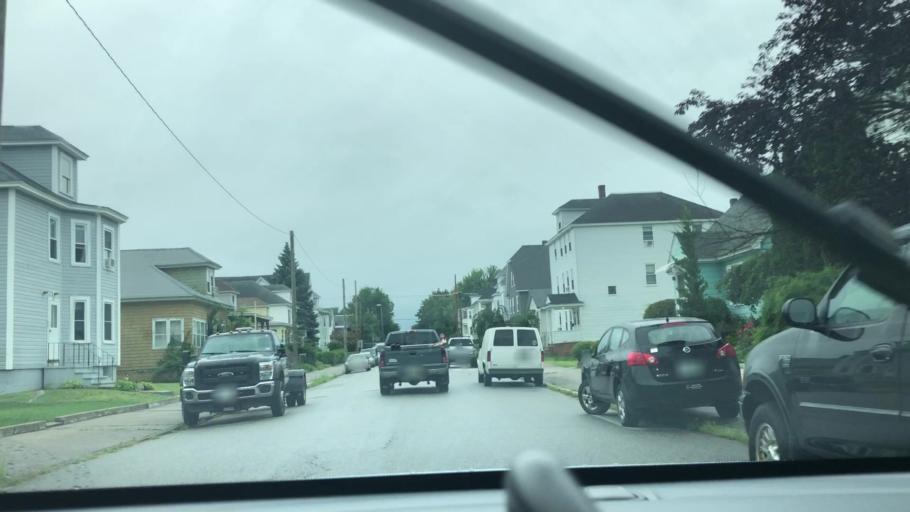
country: US
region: New Hampshire
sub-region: Hillsborough County
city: Manchester
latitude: 42.9981
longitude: -71.4809
